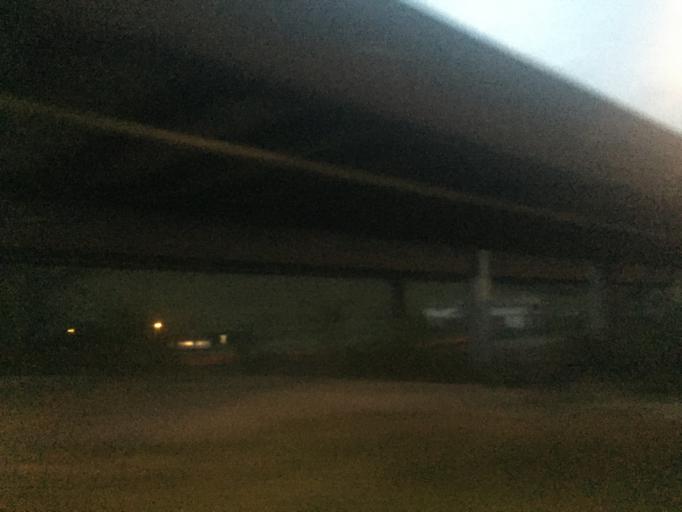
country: IT
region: The Marches
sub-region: Provincia di Macerata
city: Muccia
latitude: 43.0770
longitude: 13.0563
